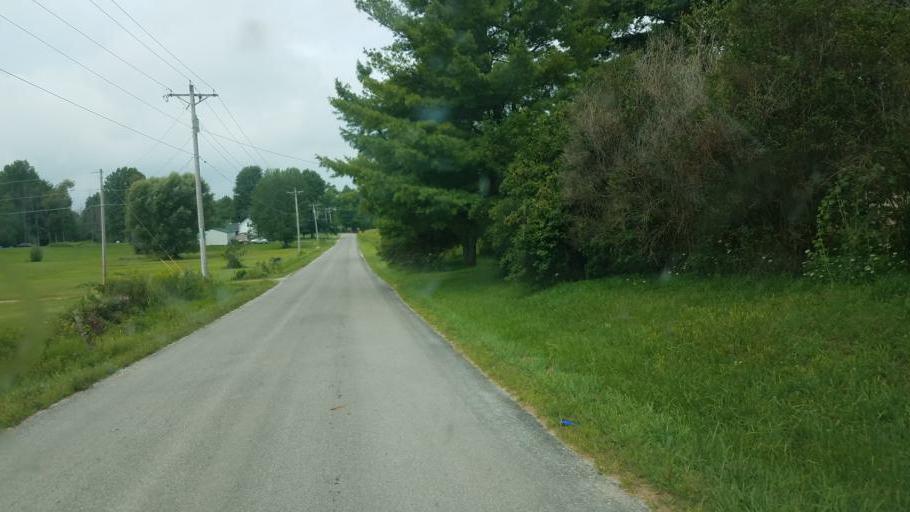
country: US
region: Ohio
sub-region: Morrow County
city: Mount Gilead
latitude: 40.4759
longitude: -82.7782
